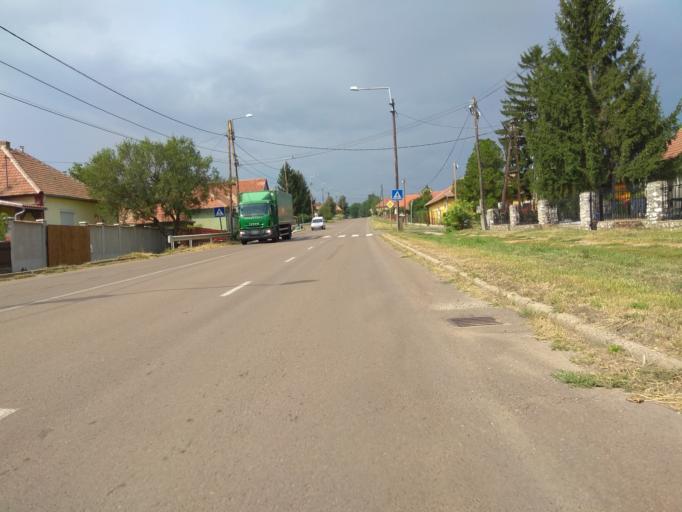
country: HU
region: Borsod-Abauj-Zemplen
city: Emod
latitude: 47.9312
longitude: 20.8115
